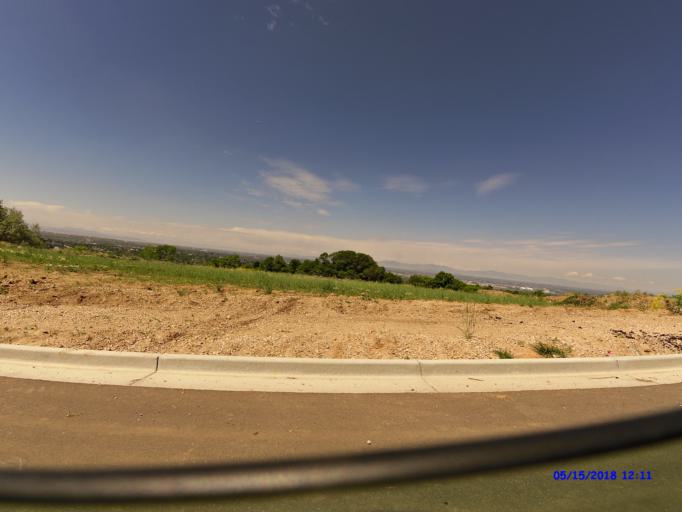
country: US
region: Utah
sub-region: Weber County
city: Uintah
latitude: 41.1803
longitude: -111.9336
